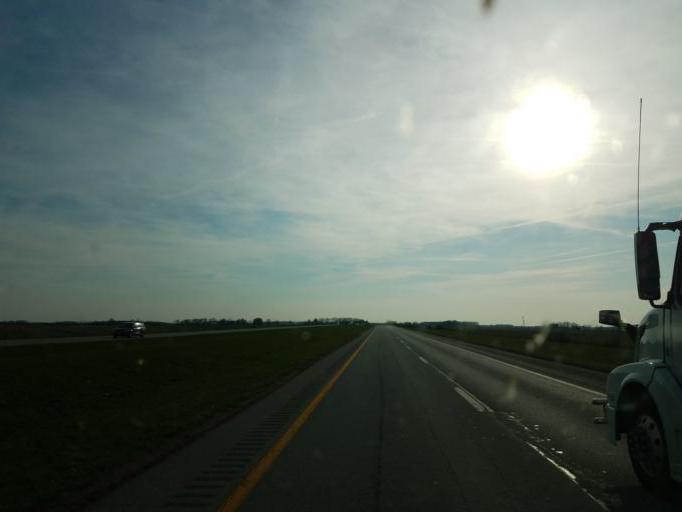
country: US
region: Ohio
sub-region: Greene County
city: Shawnee Hills
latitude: 39.5434
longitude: -83.7612
